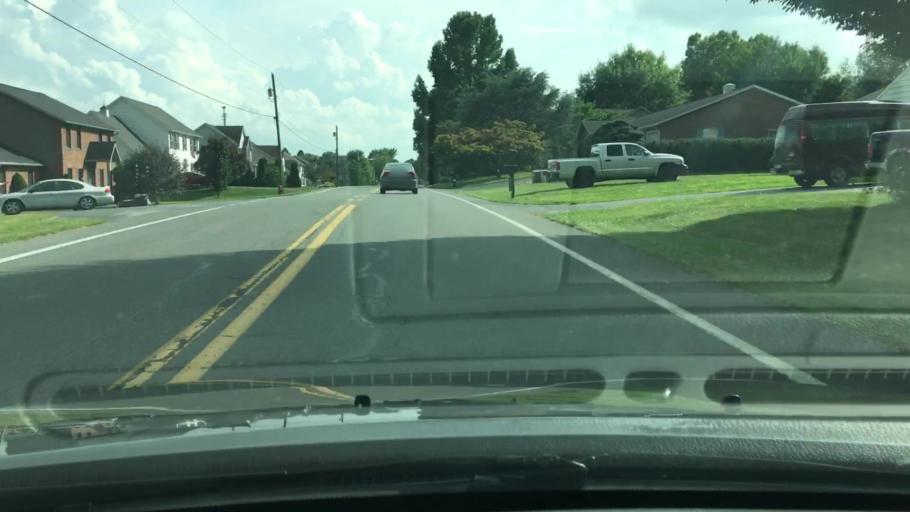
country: US
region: Pennsylvania
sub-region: Franklin County
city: Guilford
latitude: 39.9283
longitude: -77.5908
